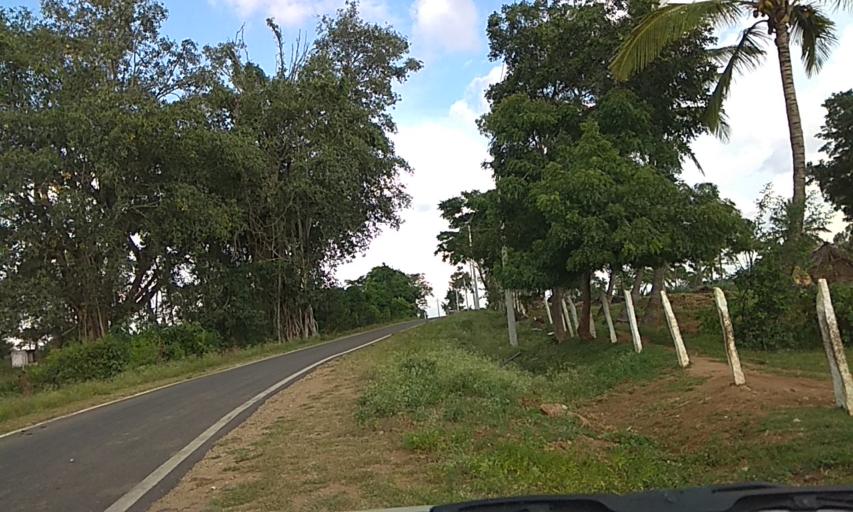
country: IN
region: Karnataka
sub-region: Chamrajnagar
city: Gundlupet
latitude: 11.7623
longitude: 76.7732
